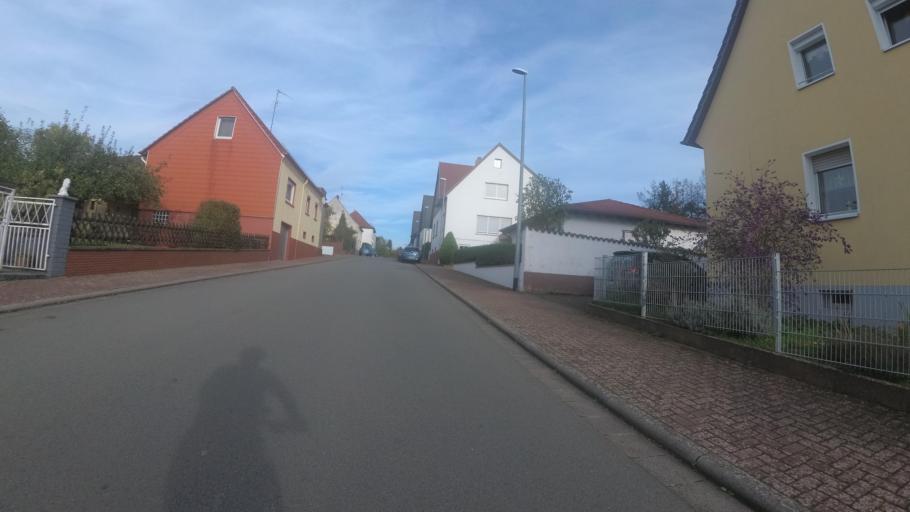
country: DE
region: Rheinland-Pfalz
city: Ramstein-Miesenbach
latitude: 49.4562
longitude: 7.5571
